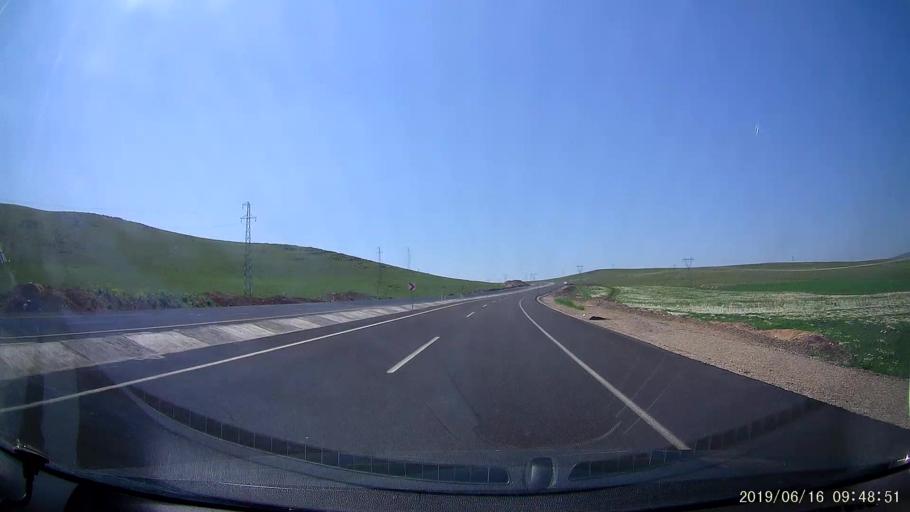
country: TR
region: Kars
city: Digor
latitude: 40.4283
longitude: 43.3559
